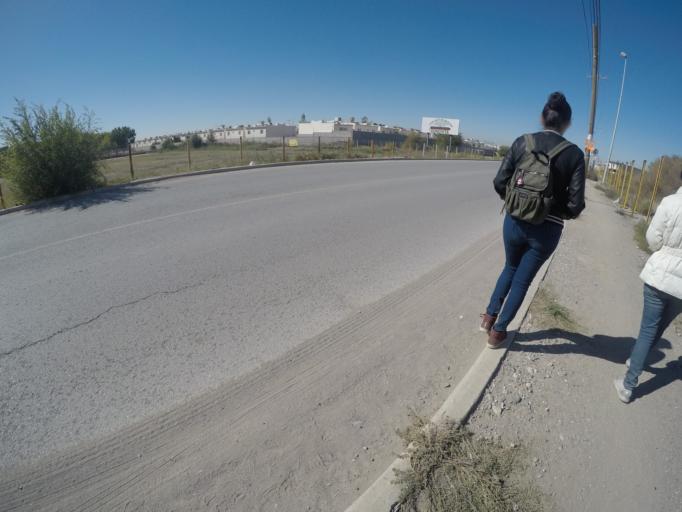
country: US
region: Texas
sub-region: El Paso County
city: Socorro
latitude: 31.6908
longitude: -106.3572
